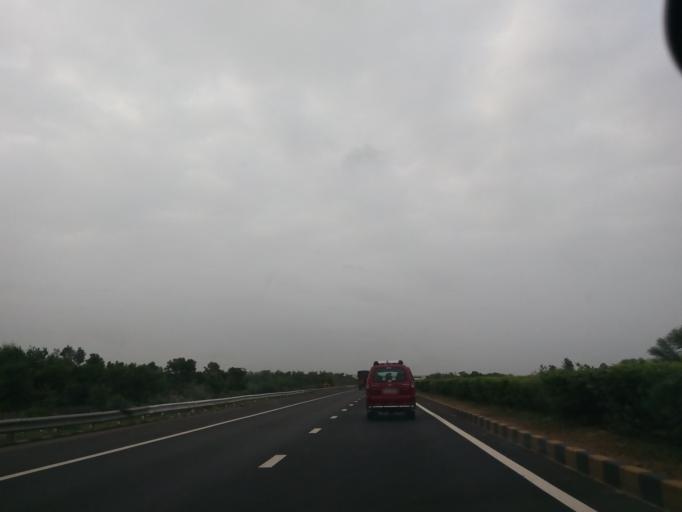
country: IN
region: Gujarat
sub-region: Kheda
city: Nadiad
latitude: 22.7863
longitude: 72.8444
